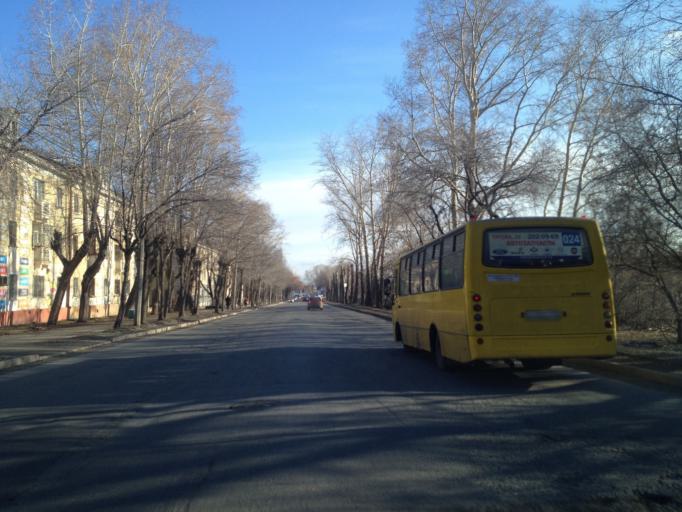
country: RU
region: Sverdlovsk
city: Sovkhoznyy
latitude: 56.7648
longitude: 60.6132
